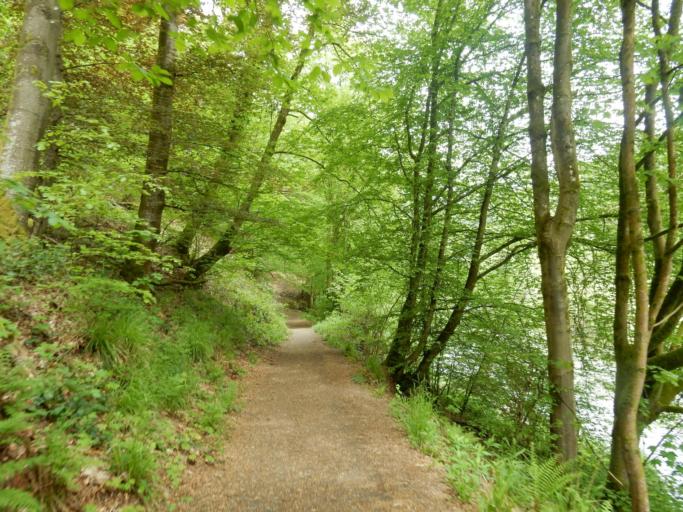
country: BE
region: Wallonia
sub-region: Province du Luxembourg
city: Bouillon
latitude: 49.7898
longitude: 5.0517
